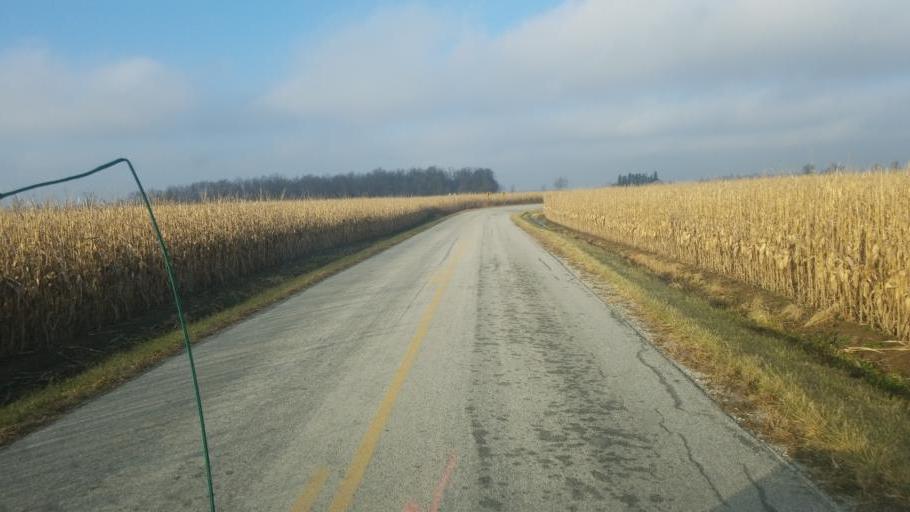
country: US
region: Ohio
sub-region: Hardin County
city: Kenton
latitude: 40.6915
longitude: -83.5951
